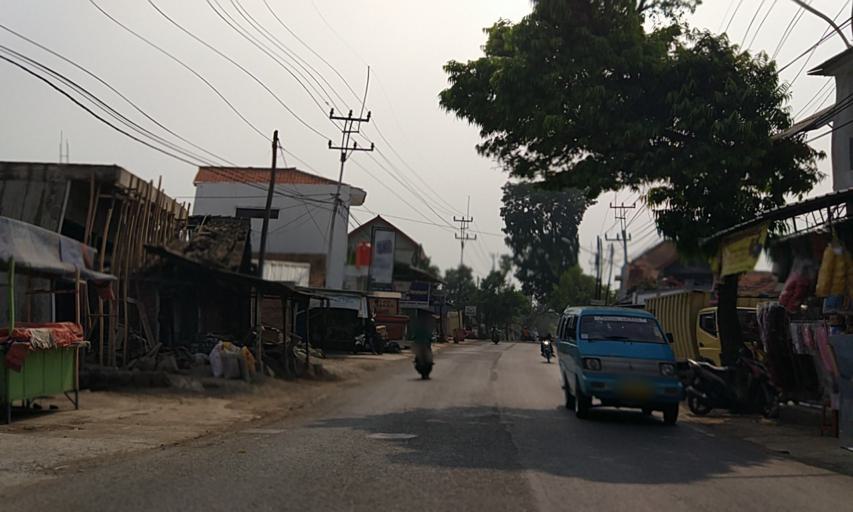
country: ID
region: West Java
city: Banjaran
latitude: -7.0432
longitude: 107.5556
